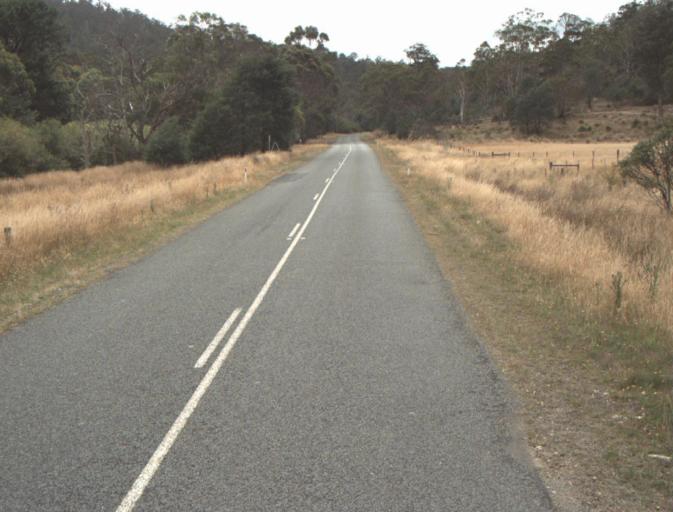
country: AU
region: Tasmania
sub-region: Northern Midlands
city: Evandale
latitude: -41.4973
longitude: 147.4184
